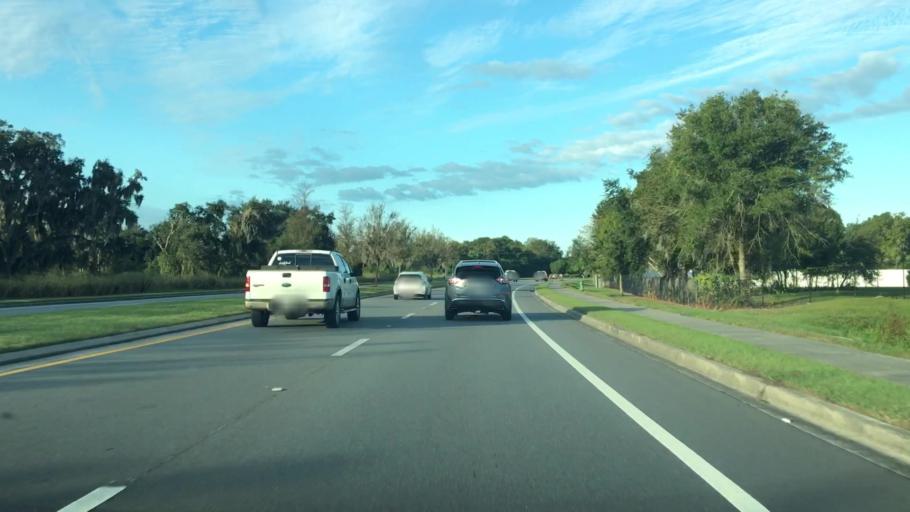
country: US
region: Florida
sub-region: Seminole County
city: Midway
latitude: 28.7609
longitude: -81.2181
